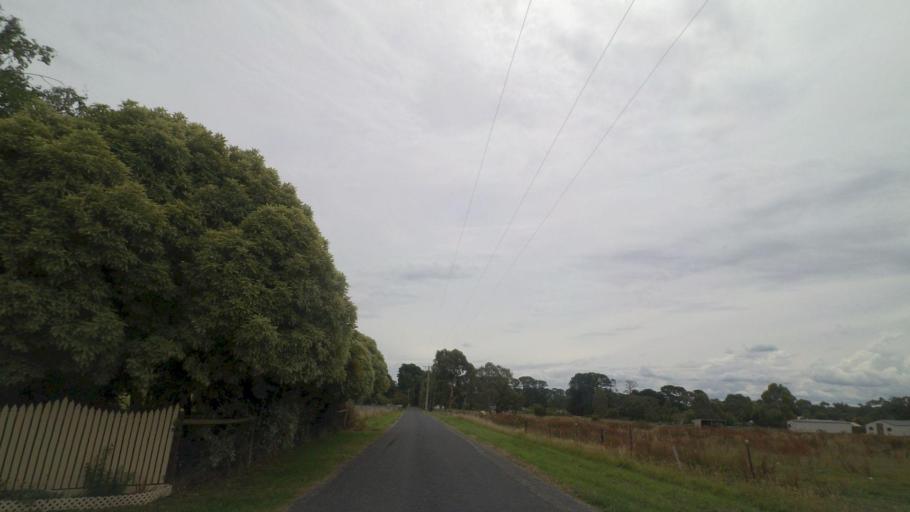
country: AU
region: Victoria
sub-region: Knox
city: The Basin
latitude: -37.8426
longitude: 145.3164
